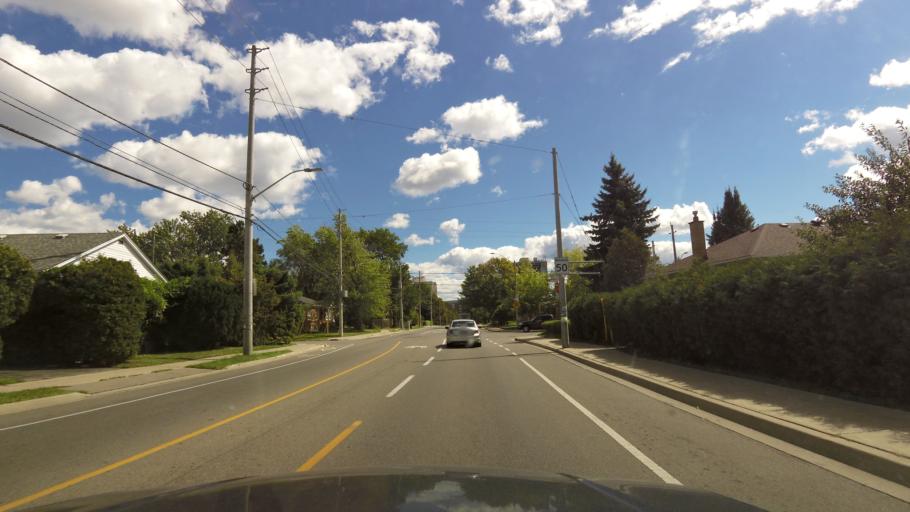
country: CA
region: Ontario
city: Mississauga
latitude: 43.5756
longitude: -79.6164
